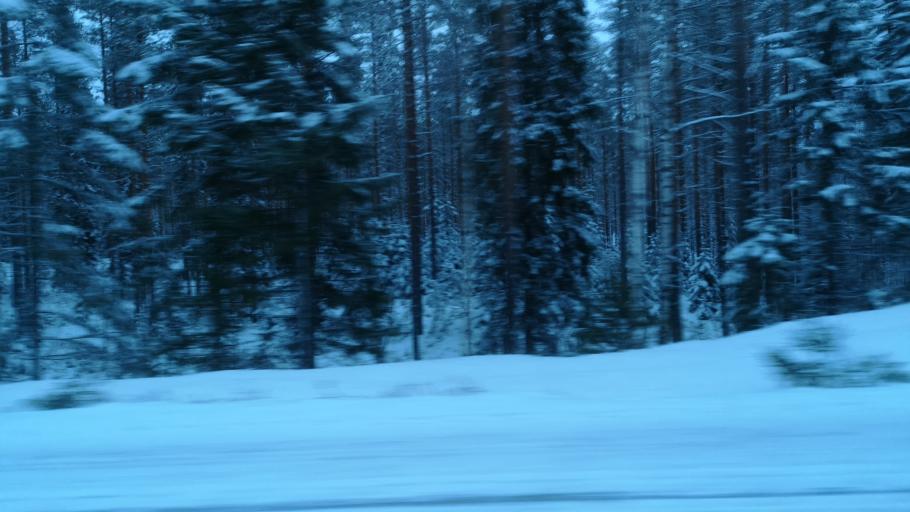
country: FI
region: Southern Savonia
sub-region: Savonlinna
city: Savonlinna
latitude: 61.9820
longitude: 28.8094
